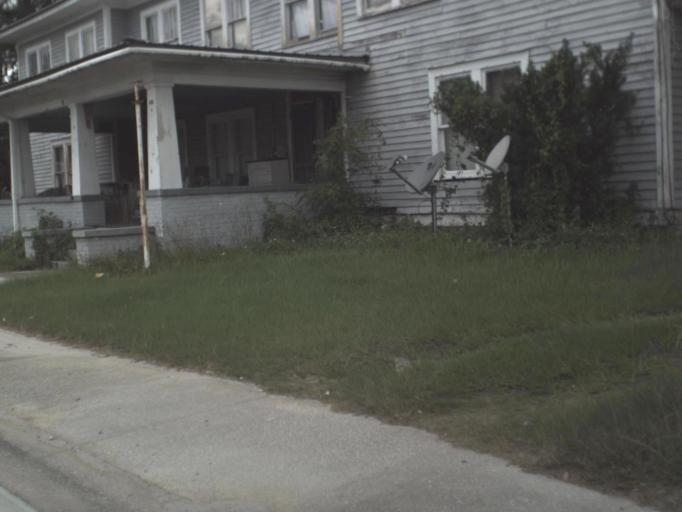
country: US
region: Florida
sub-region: Hamilton County
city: Jasper
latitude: 30.5185
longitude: -82.9502
